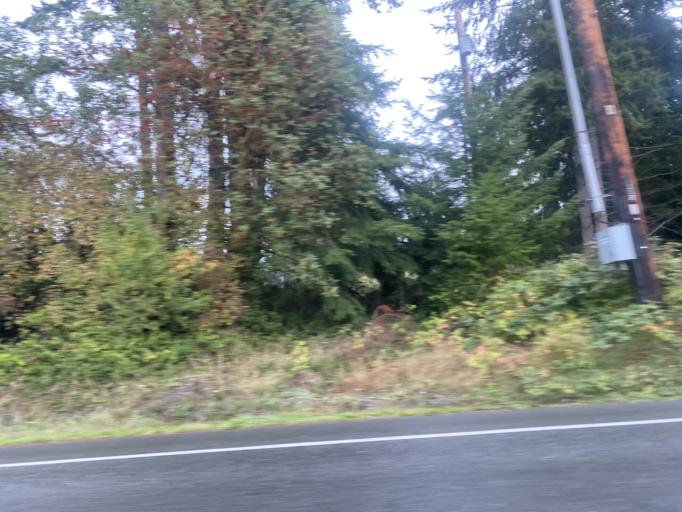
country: US
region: Washington
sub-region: Island County
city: Freeland
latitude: 48.0155
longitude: -122.5230
